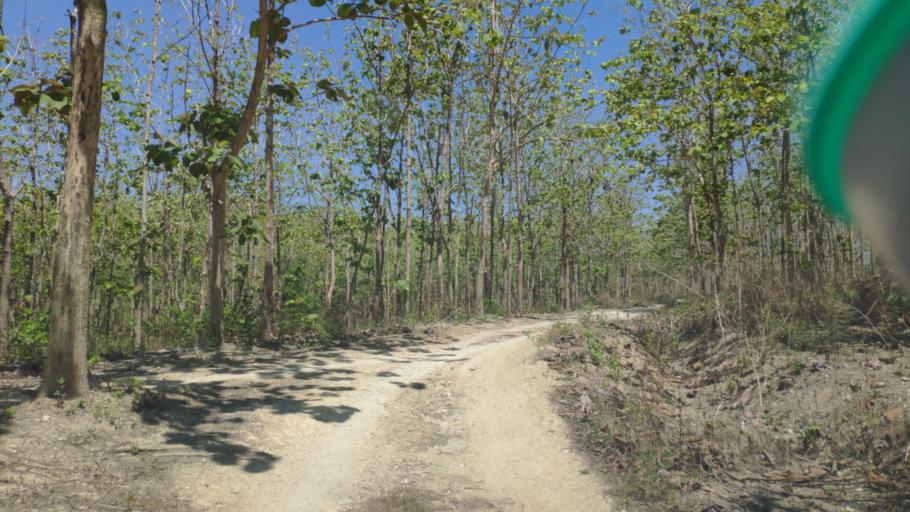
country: ID
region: Central Java
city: Suruhan
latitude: -7.0066
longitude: 111.5286
